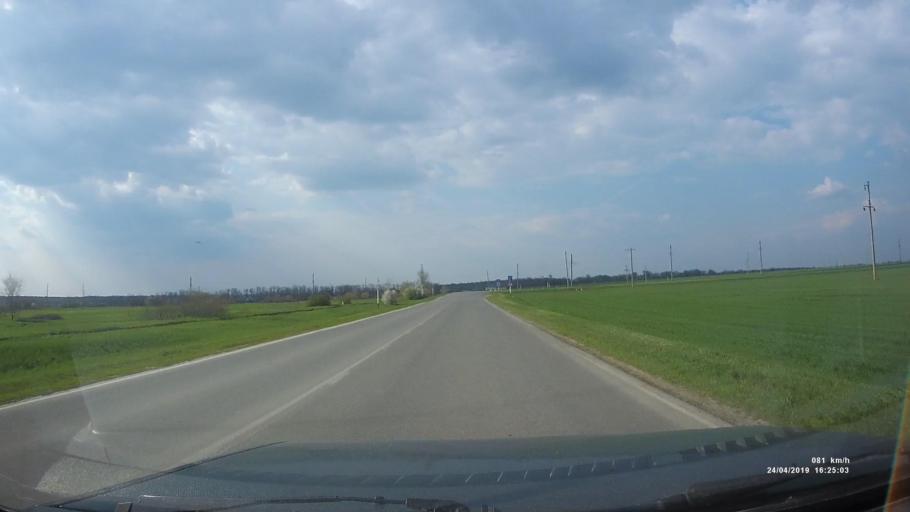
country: RU
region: Rostov
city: Orlovskiy
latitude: 46.8481
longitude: 42.0442
